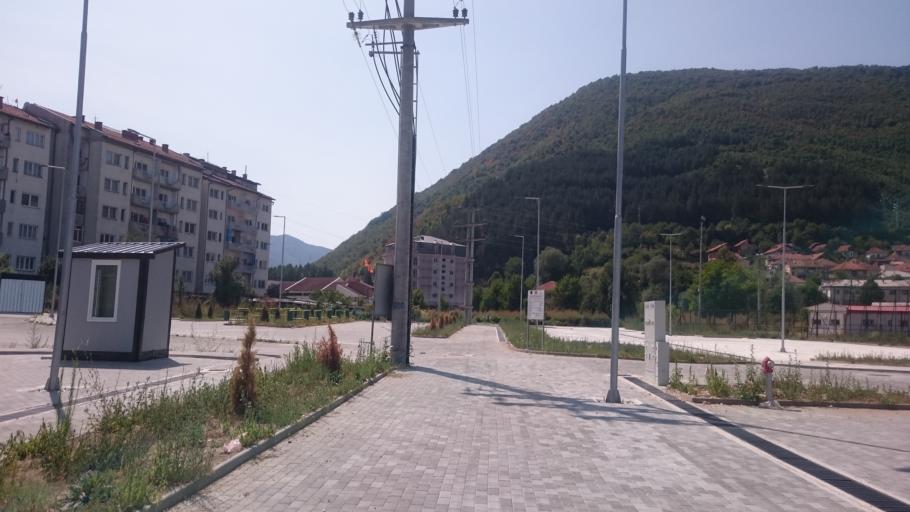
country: MK
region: Makedonski Brod
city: Makedonski Brod
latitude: 41.5087
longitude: 21.2198
